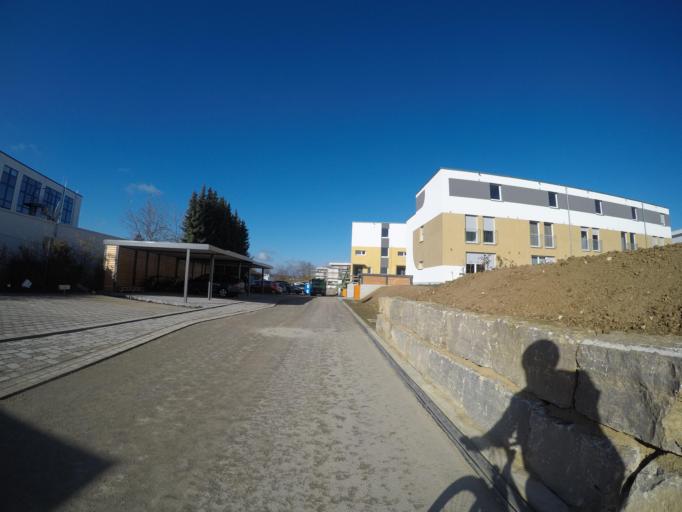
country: DE
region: Baden-Wuerttemberg
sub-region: Tuebingen Region
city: Dornstadt
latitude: 48.4722
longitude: 9.9380
